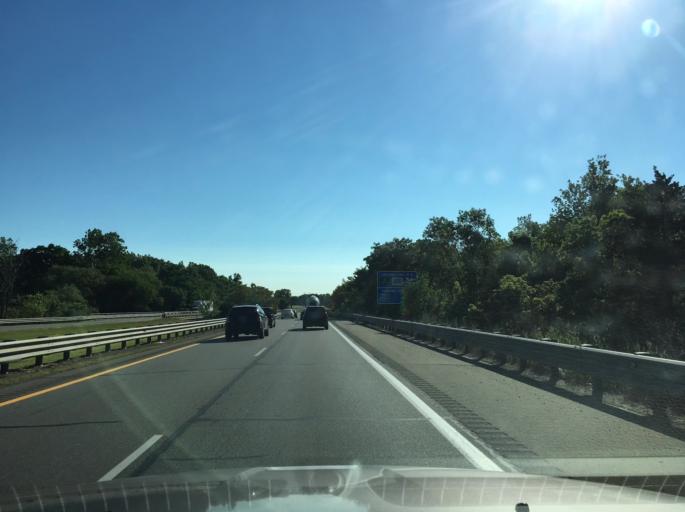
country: US
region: Michigan
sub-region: Macomb County
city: Sterling Heights
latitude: 42.6031
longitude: -83.0219
